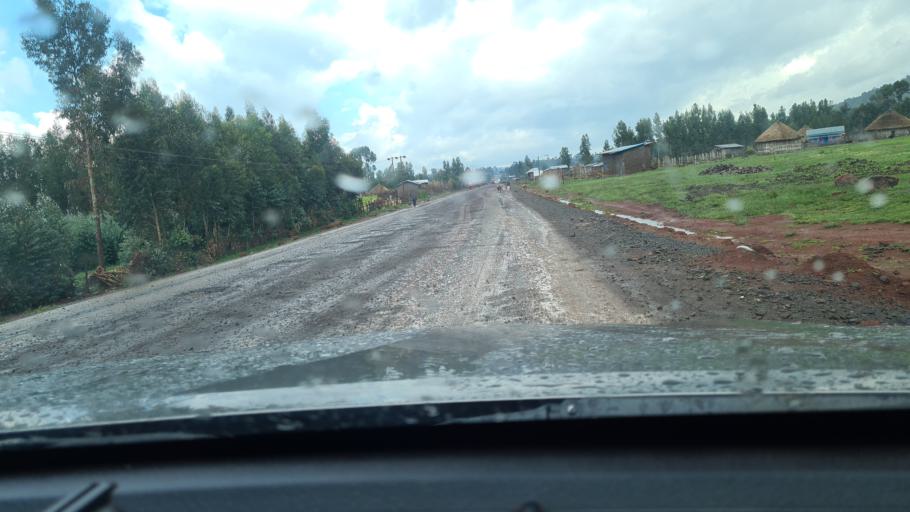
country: ET
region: Oromiya
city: Huruta
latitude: 8.0775
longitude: 39.5464
